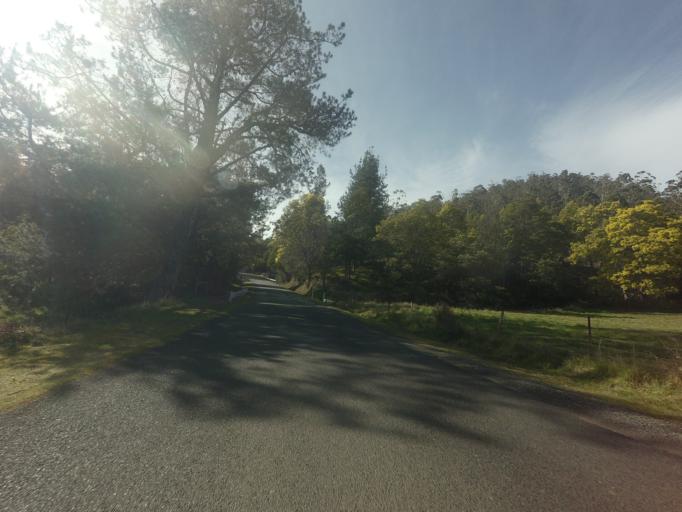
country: AU
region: Tasmania
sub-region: Huon Valley
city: Cygnet
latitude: -43.1777
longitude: 147.1491
